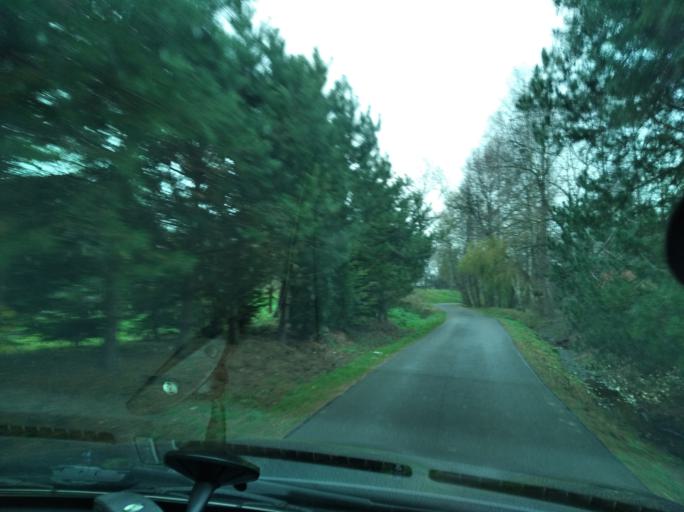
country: PL
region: Subcarpathian Voivodeship
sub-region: Powiat przeworski
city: Sietesz
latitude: 50.0021
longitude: 22.3525
